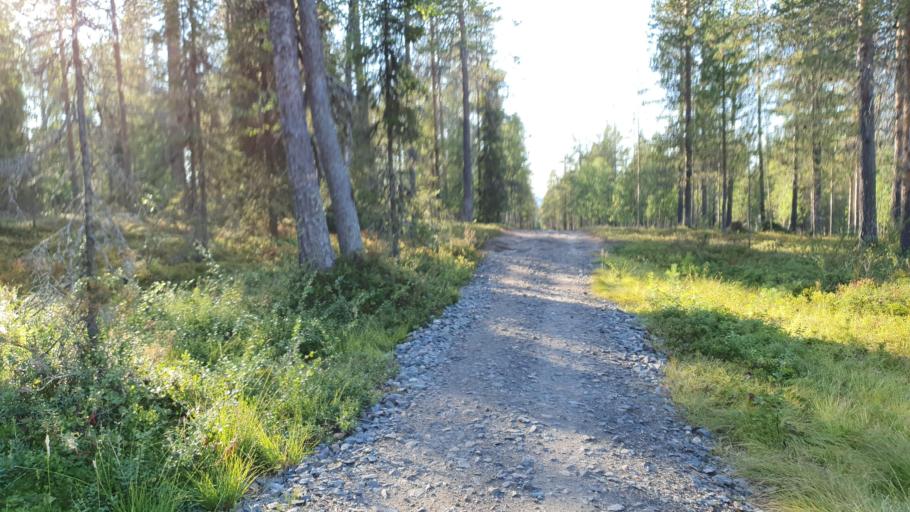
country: FI
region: Lapland
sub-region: Tunturi-Lappi
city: Kolari
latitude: 67.5992
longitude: 24.1921
